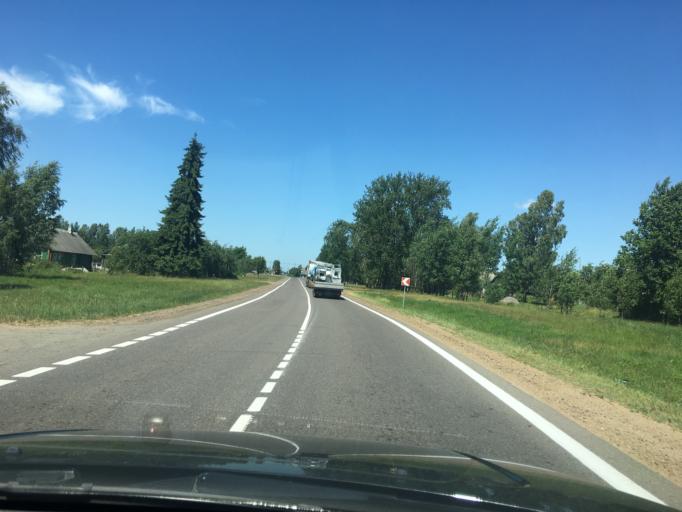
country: BY
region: Grodnenskaya
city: Iwye
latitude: 54.0579
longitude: 25.9142
